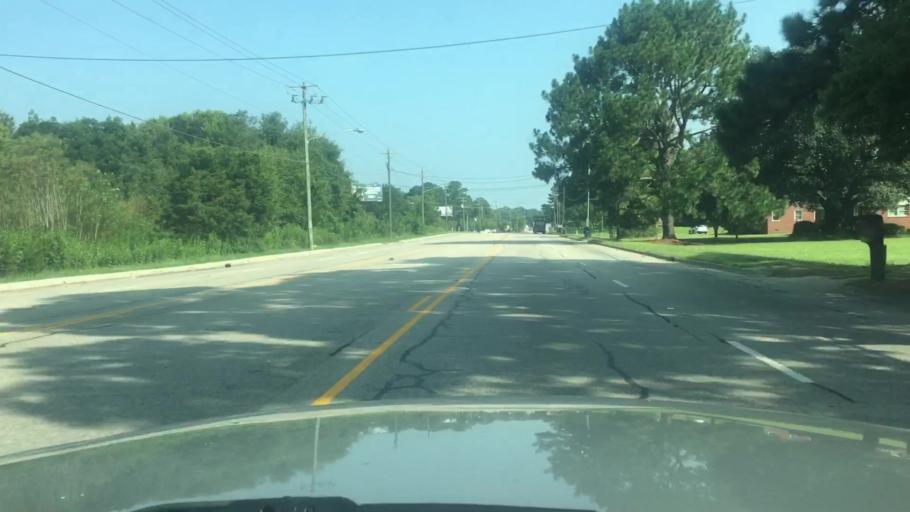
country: US
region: North Carolina
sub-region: Cumberland County
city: Vander
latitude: 35.0220
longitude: -78.8408
